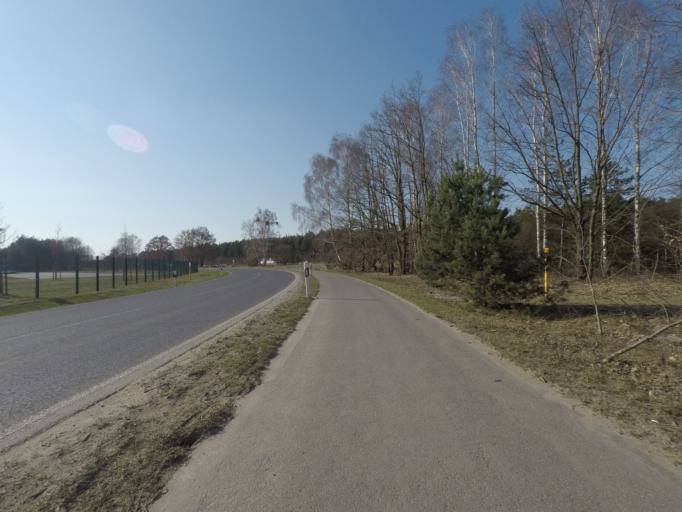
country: DE
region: Brandenburg
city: Eberswalde
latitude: 52.8521
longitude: 13.7729
